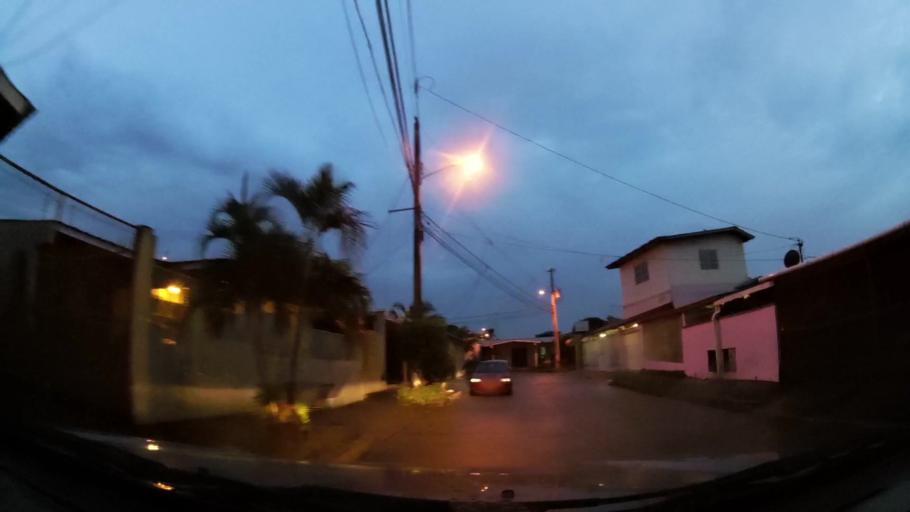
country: PA
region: Panama
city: Panama
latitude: 9.0401
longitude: -79.5196
